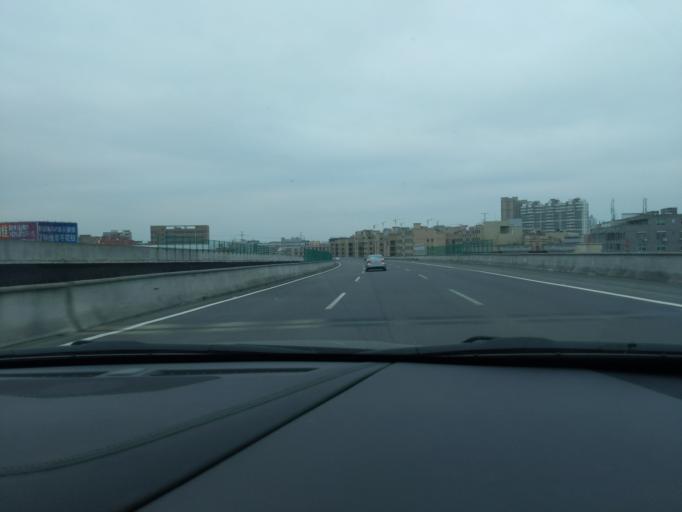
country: CN
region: Fujian
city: Shishi
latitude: 24.7549
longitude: 118.6072
